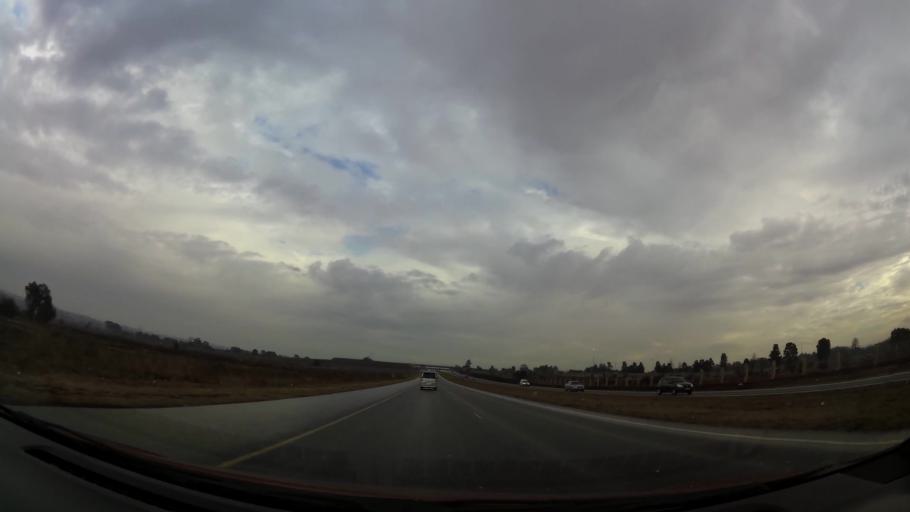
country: ZA
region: Gauteng
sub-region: City of Johannesburg Metropolitan Municipality
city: Soweto
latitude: -26.3012
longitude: 27.8566
